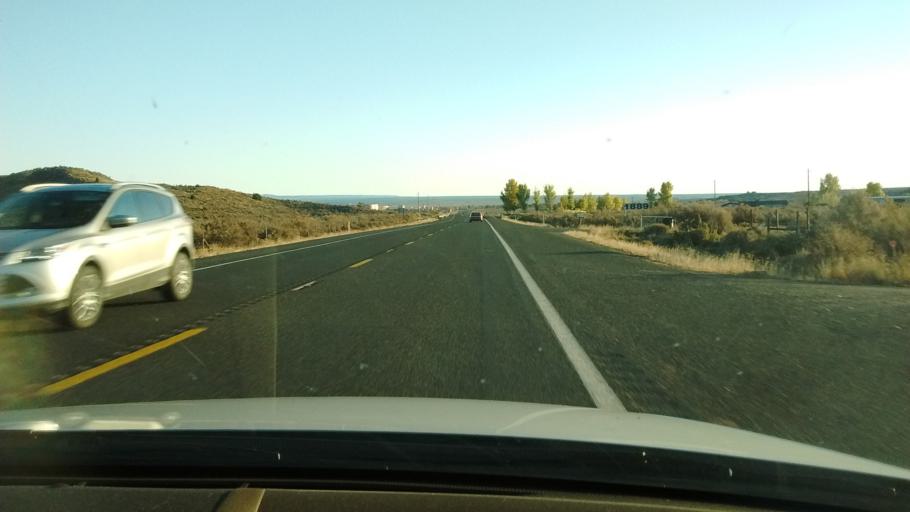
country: US
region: Arizona
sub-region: Coconino County
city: Fredonia
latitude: 36.9828
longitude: -112.5295
